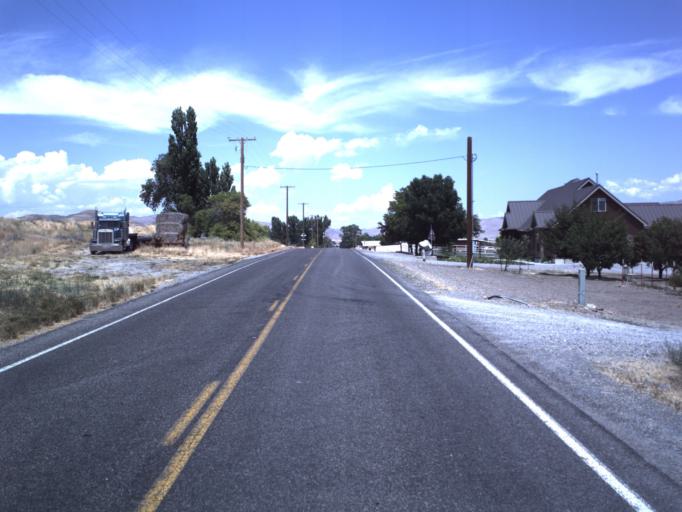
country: US
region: Utah
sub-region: Box Elder County
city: Tremonton
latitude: 41.6651
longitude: -112.2964
